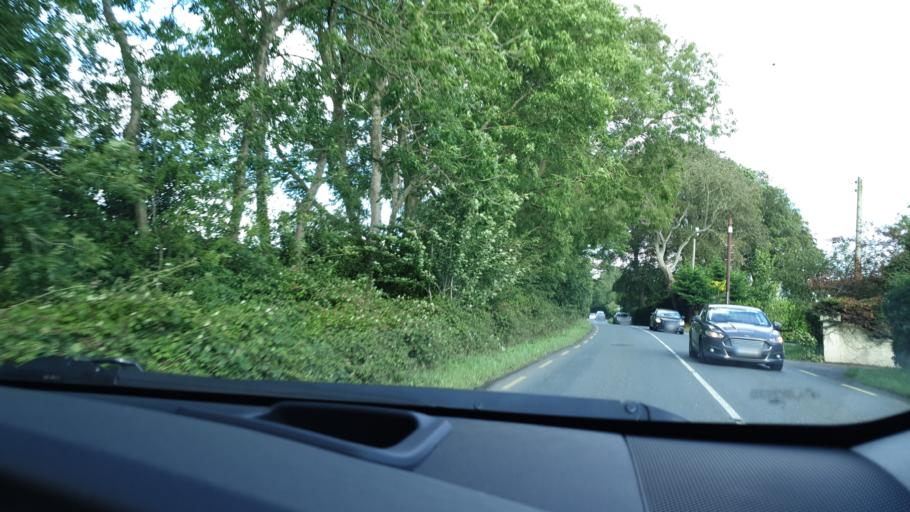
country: IE
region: Leinster
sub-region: An Mhi
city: Ashbourne
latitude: 53.4957
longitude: -6.3953
